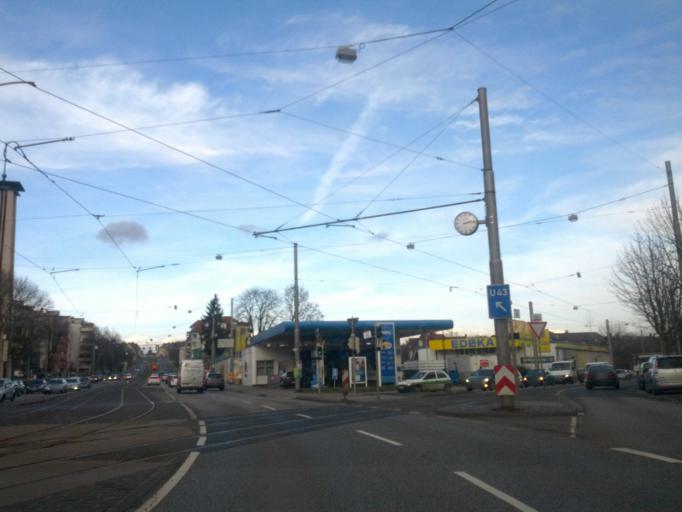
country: DE
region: Hesse
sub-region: Regierungsbezirk Kassel
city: Kassel
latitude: 51.3233
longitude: 9.5130
